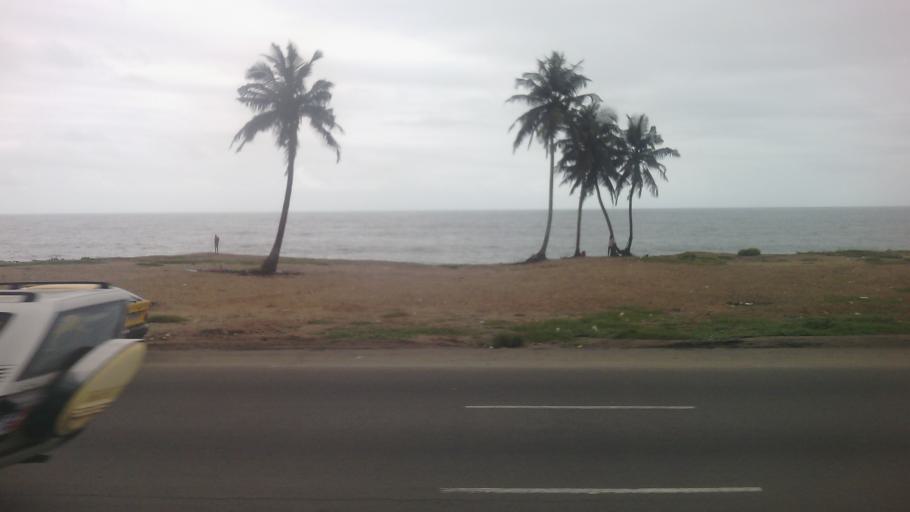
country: CI
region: Lagunes
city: Bingerville
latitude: 5.2410
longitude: -3.9070
